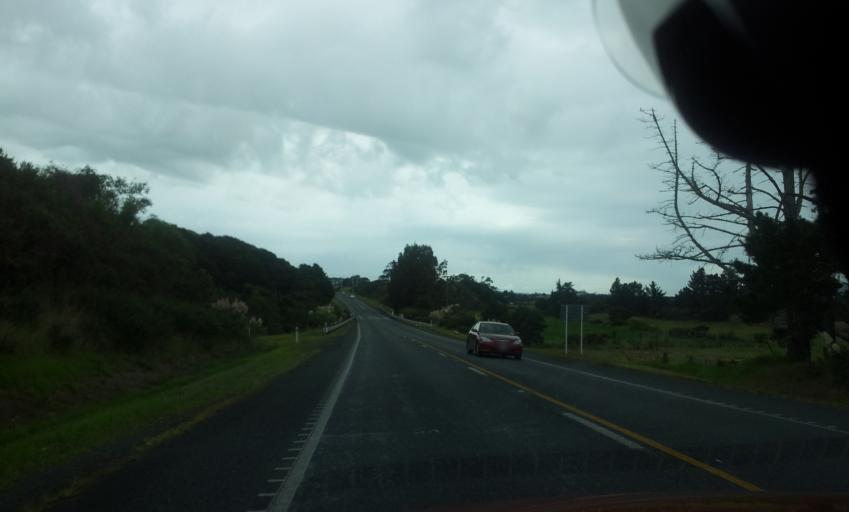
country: NZ
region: Northland
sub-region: Whangarei
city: Ruakaka
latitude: -35.9211
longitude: 174.4532
